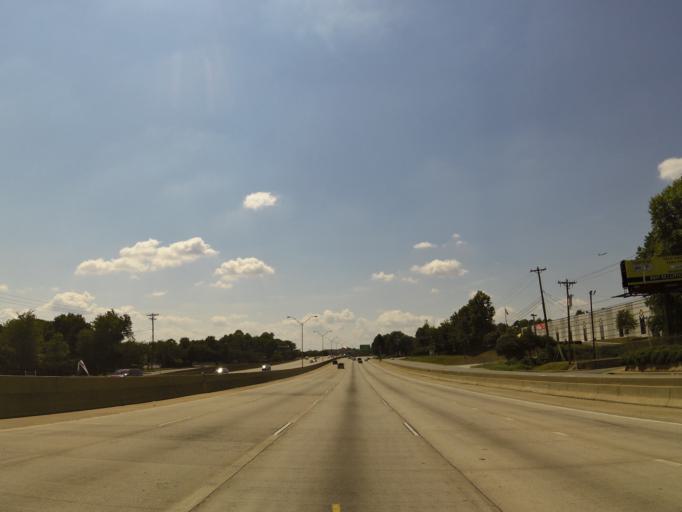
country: US
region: North Carolina
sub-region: Mecklenburg County
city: Charlotte
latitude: 35.2398
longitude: -80.9093
